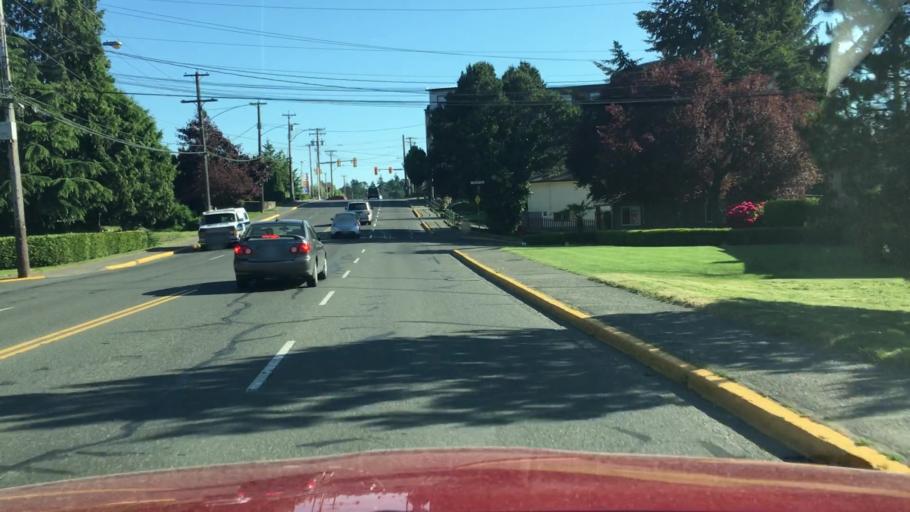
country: CA
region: British Columbia
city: Victoria
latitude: 48.4435
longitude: -123.4018
